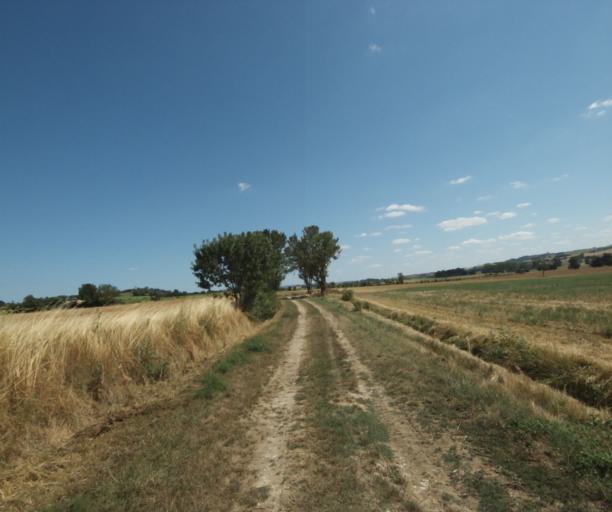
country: FR
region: Midi-Pyrenees
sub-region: Departement de la Haute-Garonne
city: Saint-Felix-Lauragais
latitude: 43.4961
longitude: 1.8752
